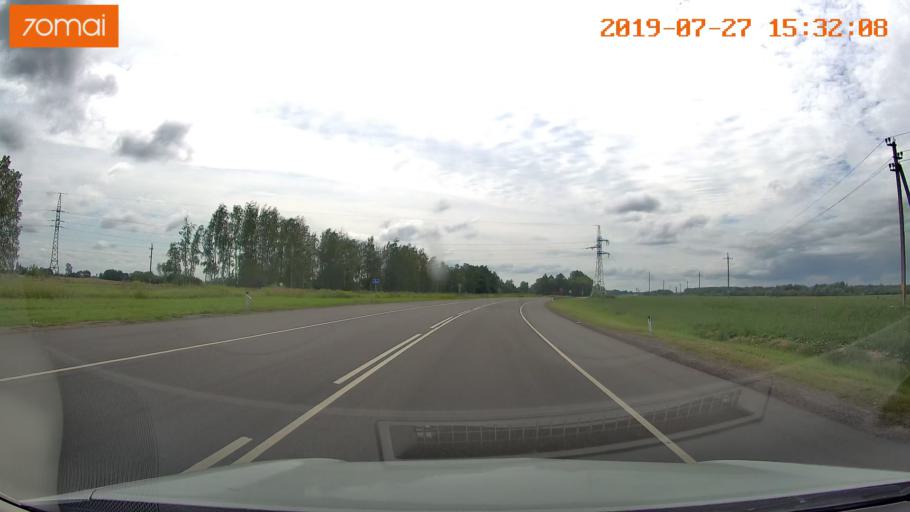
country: RU
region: Kaliningrad
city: Nesterov
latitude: 54.6175
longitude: 22.4785
